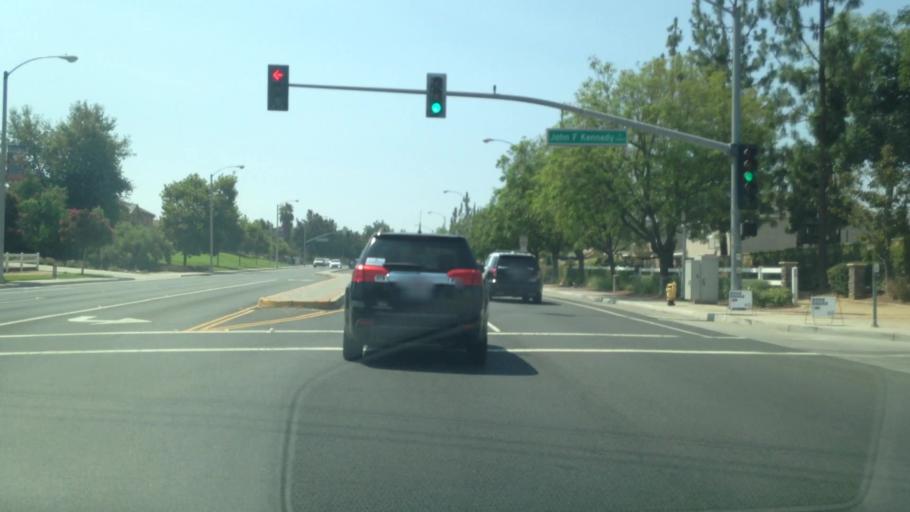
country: US
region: California
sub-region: Riverside County
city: Woodcrest
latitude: 33.9020
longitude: -117.3263
